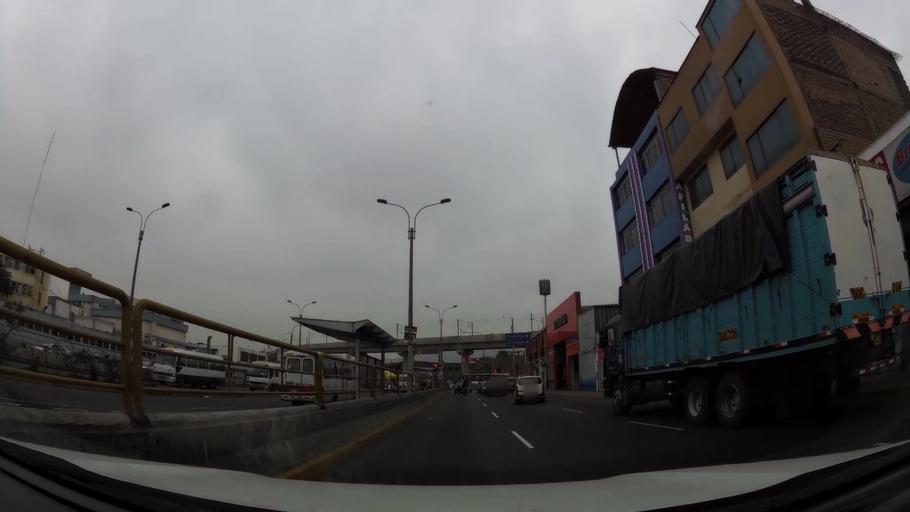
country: PE
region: Lima
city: Lima
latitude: -12.0571
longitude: -77.0155
